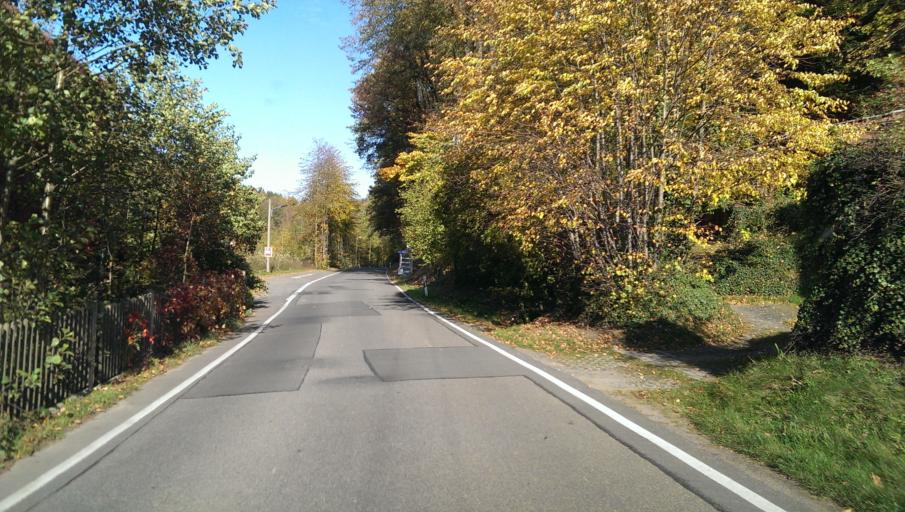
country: DE
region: Saxony
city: Waldheim
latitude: 51.0635
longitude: 13.0106
